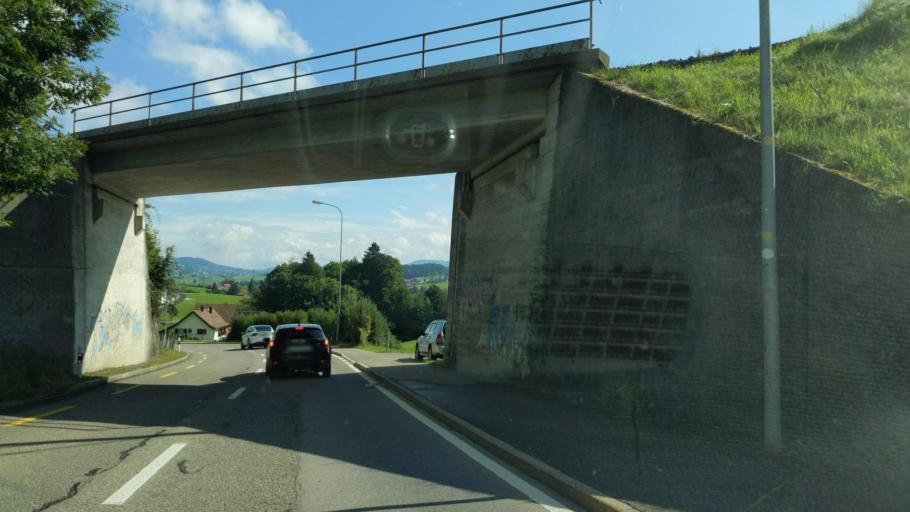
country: CH
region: Appenzell Ausserrhoden
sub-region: Bezirk Hinterland
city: Waldstatt
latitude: 47.3599
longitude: 9.2897
